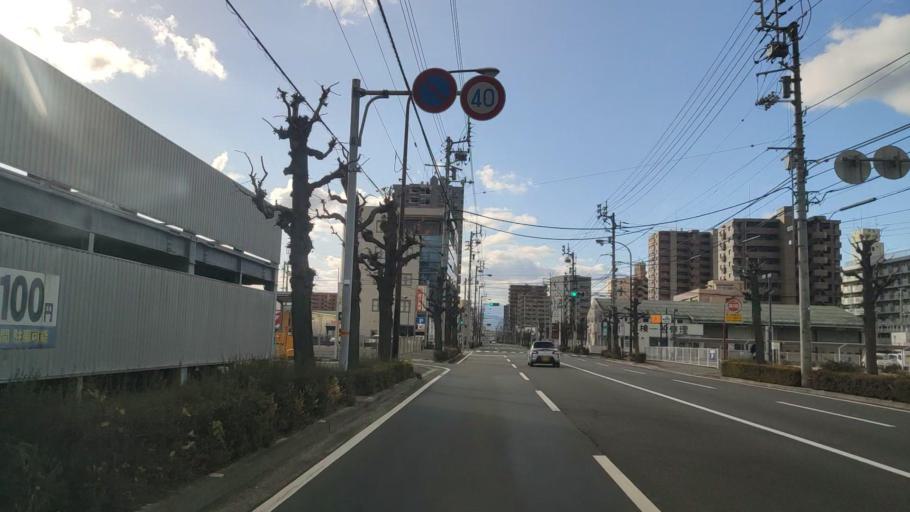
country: JP
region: Ehime
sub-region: Shikoku-chuo Shi
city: Matsuyama
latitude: 33.8362
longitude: 132.7525
